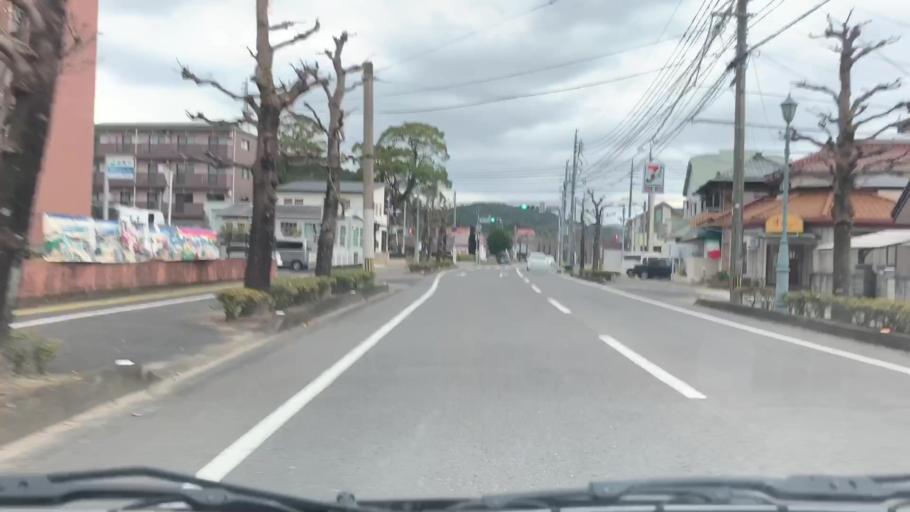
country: JP
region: Saga Prefecture
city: Ureshinomachi-shimojuku
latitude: 33.1016
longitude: 129.9870
